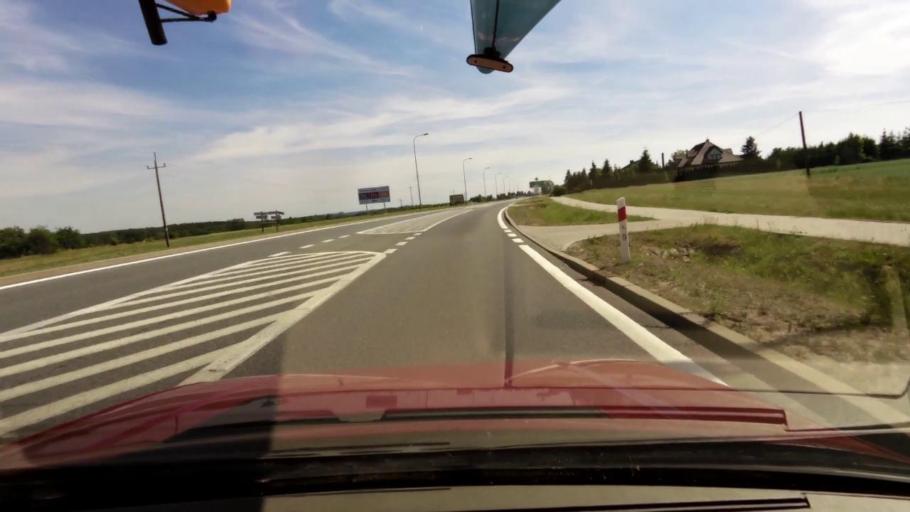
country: PL
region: Pomeranian Voivodeship
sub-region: Powiat slupski
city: Kobylnica
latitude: 54.4283
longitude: 17.0069
